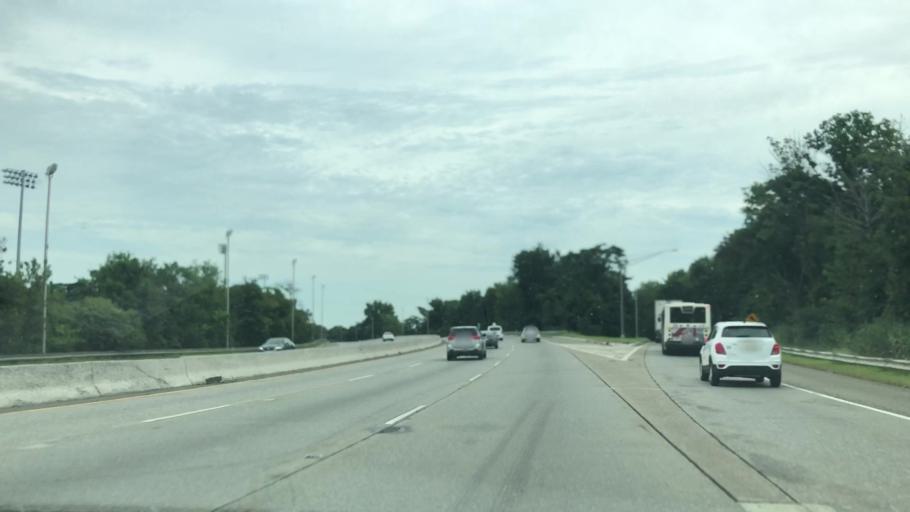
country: US
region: New Jersey
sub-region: Bergen County
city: Wallington
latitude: 40.8483
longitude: -74.1215
